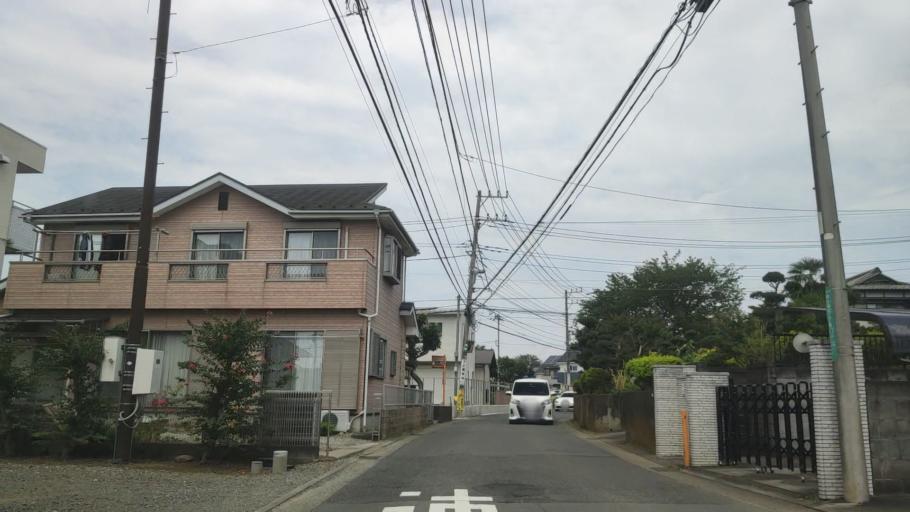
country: JP
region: Kanagawa
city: Atsugi
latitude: 35.4263
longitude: 139.3964
